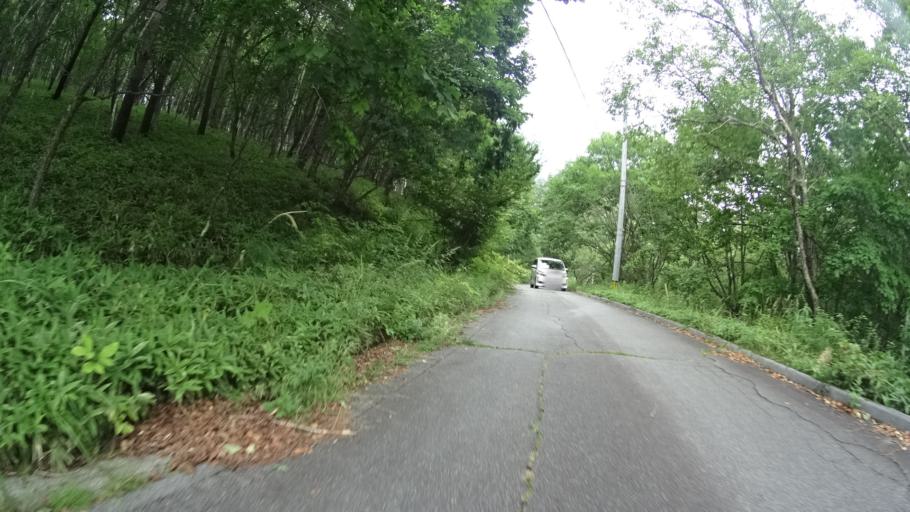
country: JP
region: Yamanashi
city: Enzan
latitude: 35.7997
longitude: 138.6354
